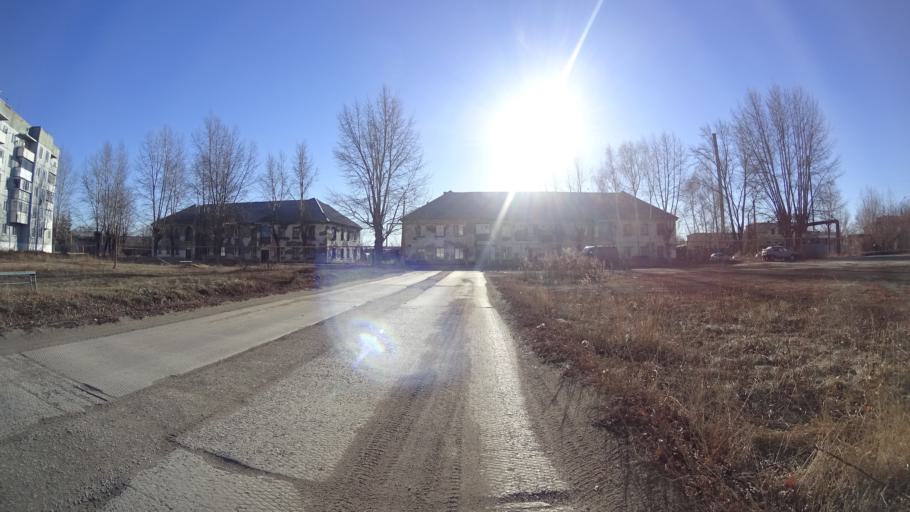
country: RU
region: Chelyabinsk
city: Troitsk
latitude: 54.1081
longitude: 61.5545
